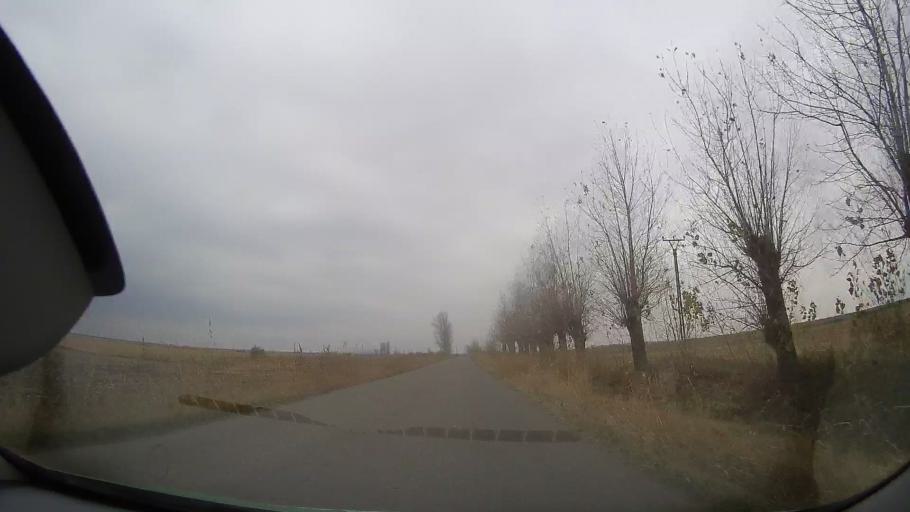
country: RO
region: Buzau
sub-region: Comuna Scutelnici
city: Scutelnici
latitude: 44.8765
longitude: 26.9425
